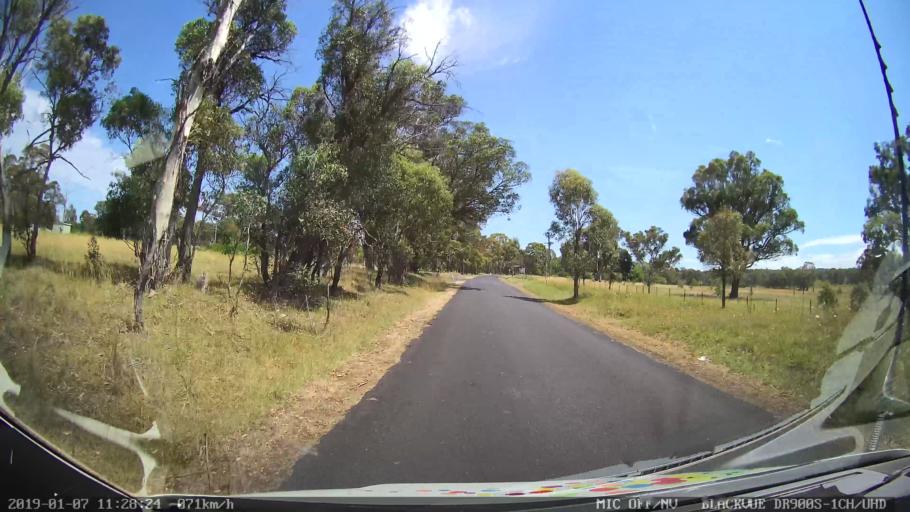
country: AU
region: New South Wales
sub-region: Armidale Dumaresq
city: Armidale
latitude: -30.4490
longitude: 151.5665
